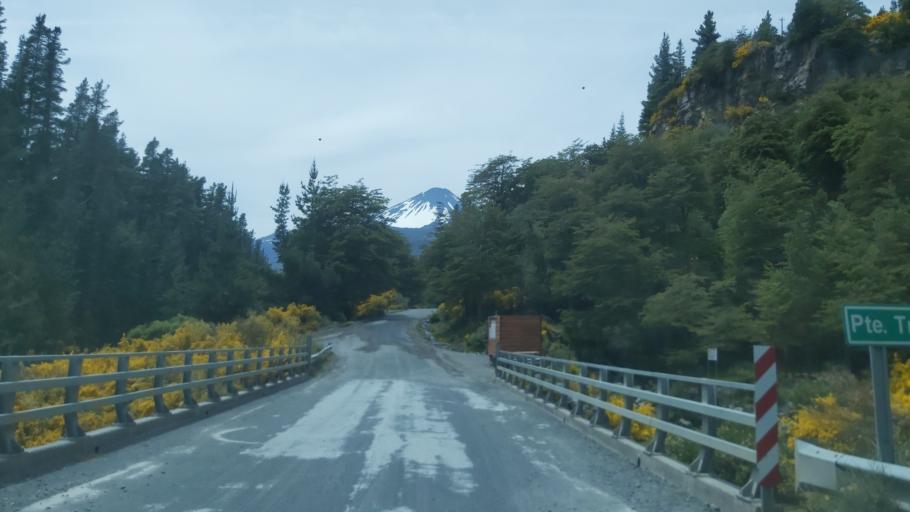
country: AR
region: Neuquen
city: Las Ovejas
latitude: -37.3965
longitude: -71.4554
